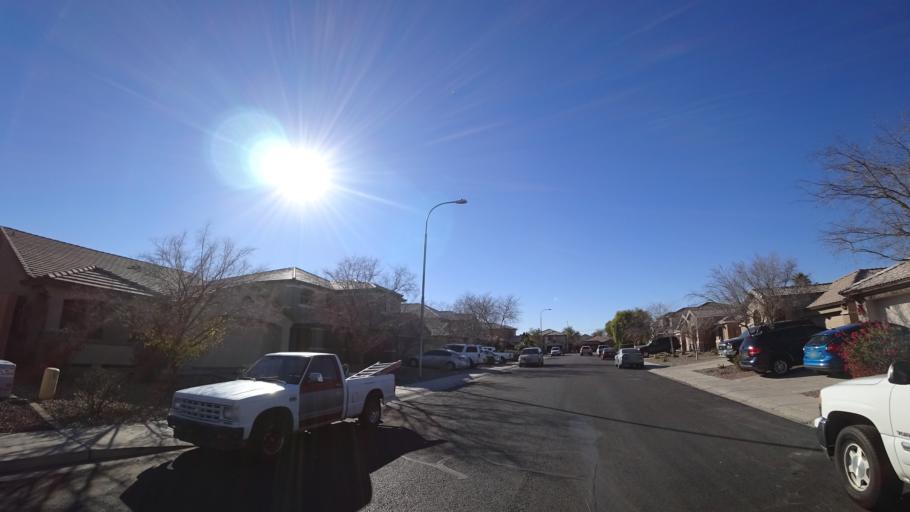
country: US
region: Arizona
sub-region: Maricopa County
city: Avondale
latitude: 33.4348
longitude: -112.3133
